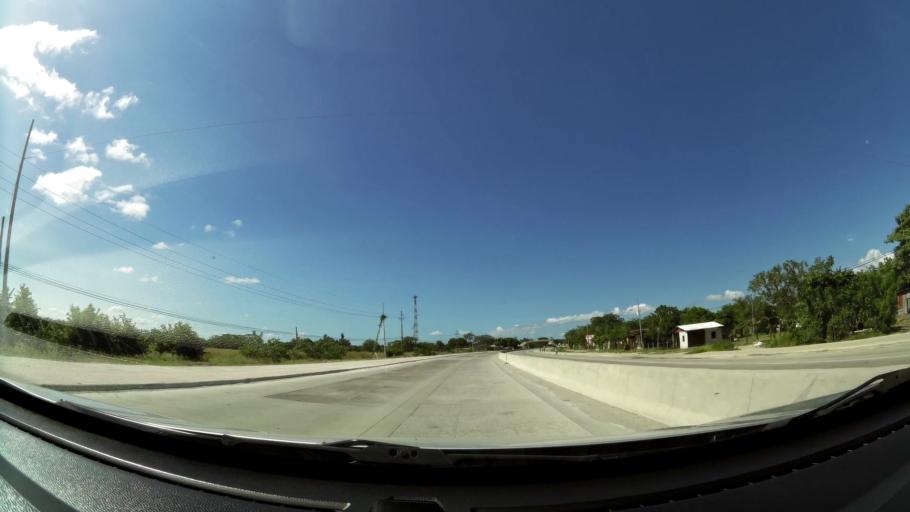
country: CR
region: Guanacaste
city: Bagaces
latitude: 10.5429
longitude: -85.3491
